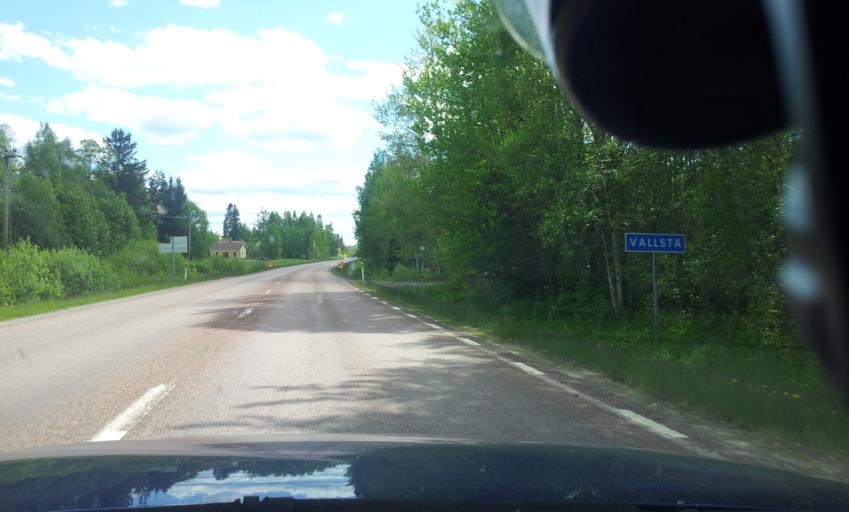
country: SE
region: Gaevleborg
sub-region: Bollnas Kommun
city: Arbra
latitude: 61.5249
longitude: 16.3640
